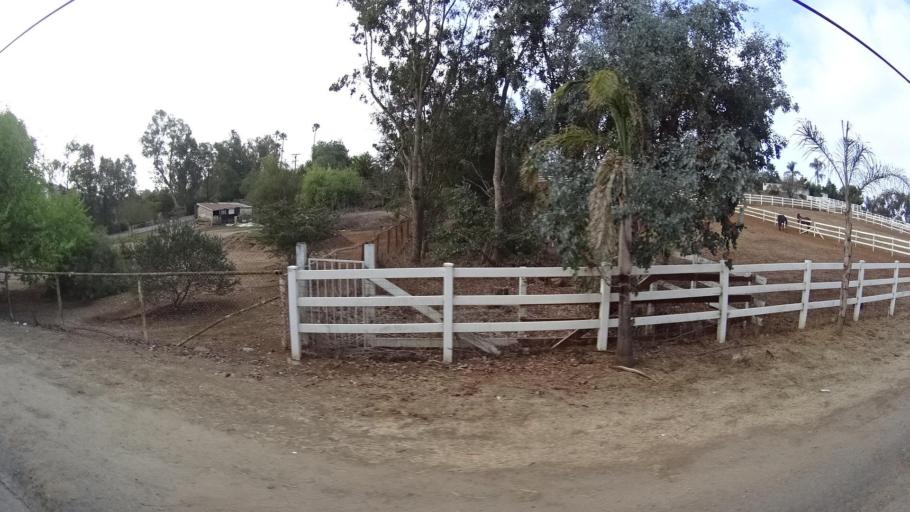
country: US
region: California
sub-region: San Diego County
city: San Marcos
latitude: 33.1798
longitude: -117.1622
